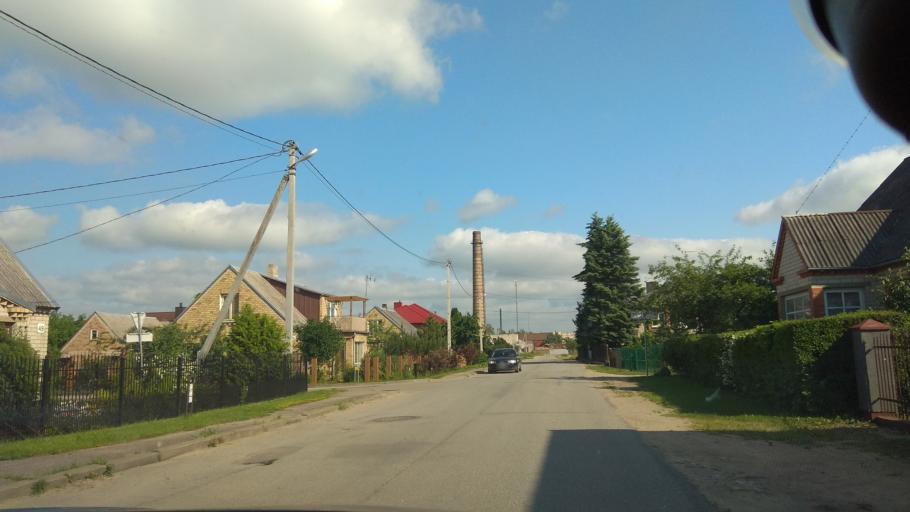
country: LT
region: Siauliu apskritis
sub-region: Joniskis
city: Joniskis
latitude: 56.2454
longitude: 23.6253
